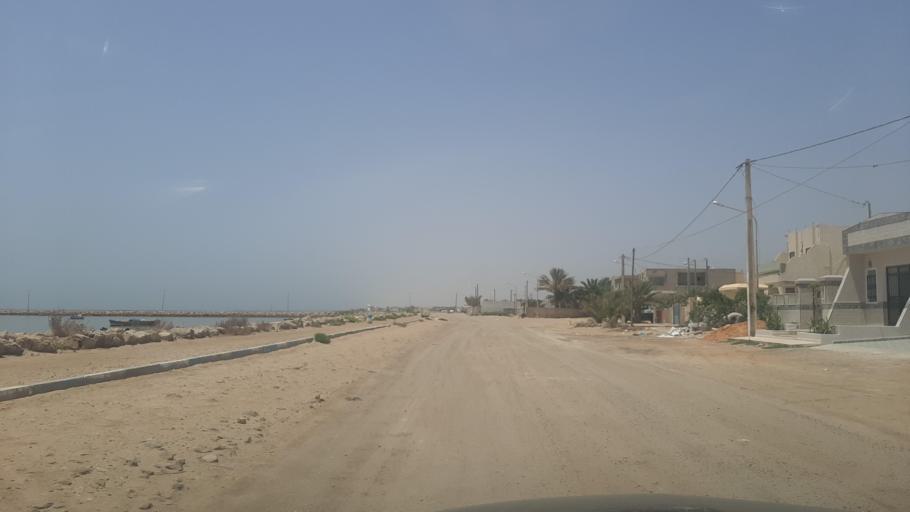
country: TN
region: Safaqis
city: Al Qarmadah
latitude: 34.6986
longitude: 11.1942
